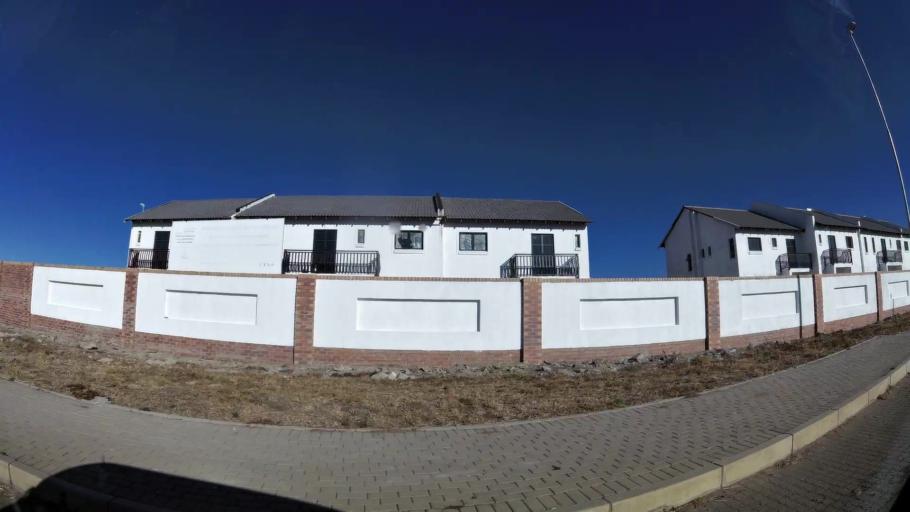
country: ZA
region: Limpopo
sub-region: Capricorn District Municipality
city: Polokwane
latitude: -23.8792
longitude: 29.4739
